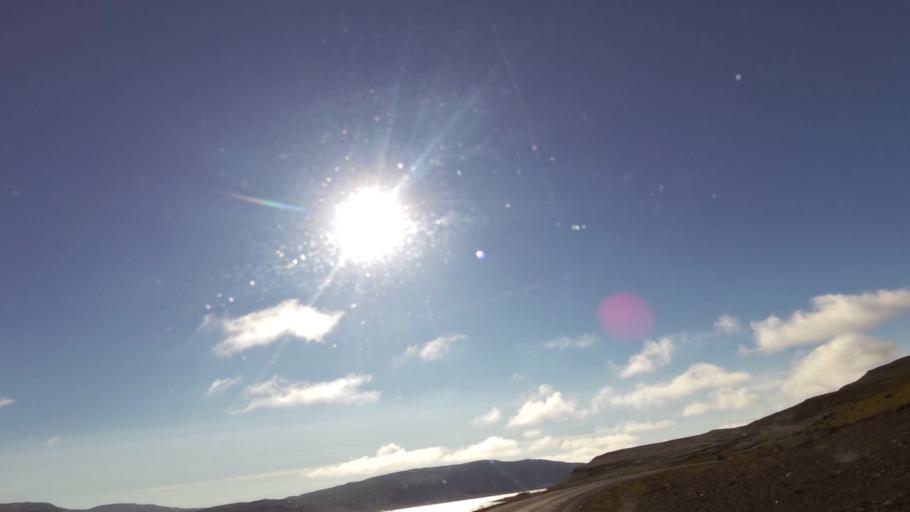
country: IS
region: West
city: Olafsvik
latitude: 65.5379
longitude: -23.8545
